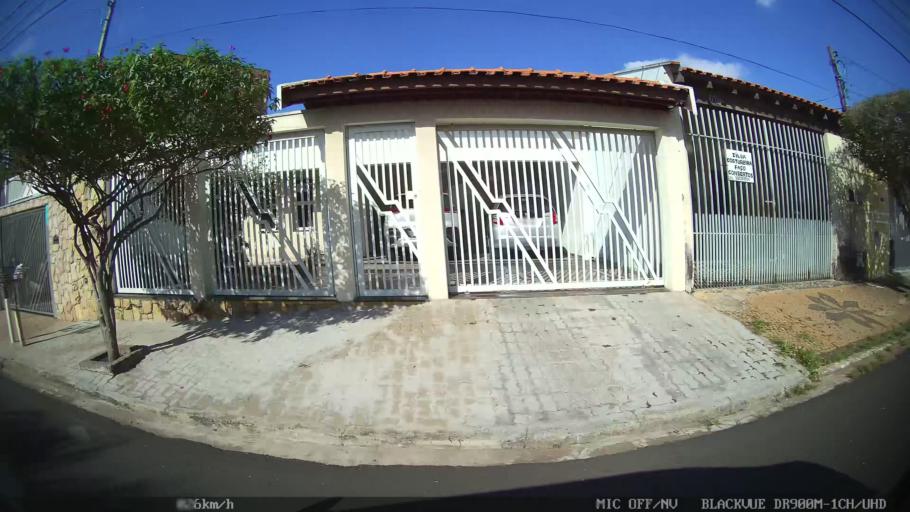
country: BR
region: Sao Paulo
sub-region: Sumare
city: Sumare
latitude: -22.8132
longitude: -47.2856
